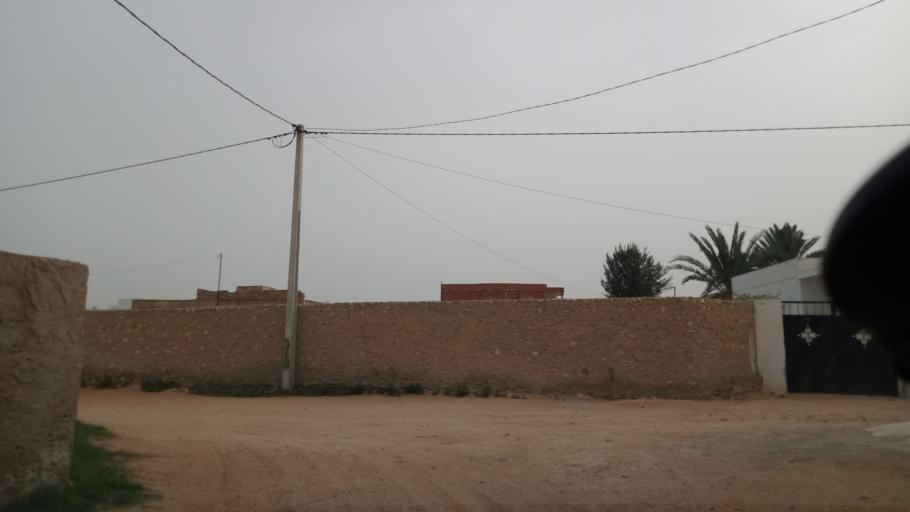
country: TN
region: Safaqis
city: Al Qarmadah
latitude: 34.7935
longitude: 10.7678
